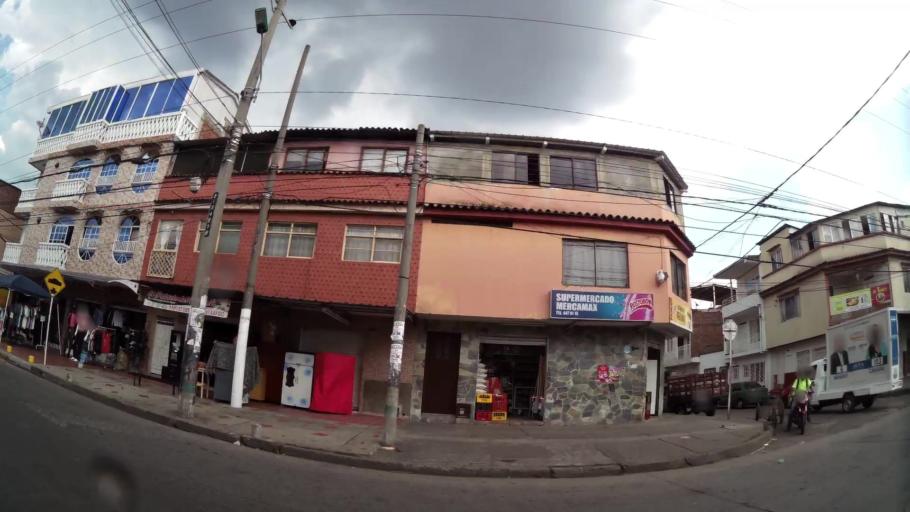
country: CO
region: Valle del Cauca
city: Cali
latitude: 3.4748
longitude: -76.5093
